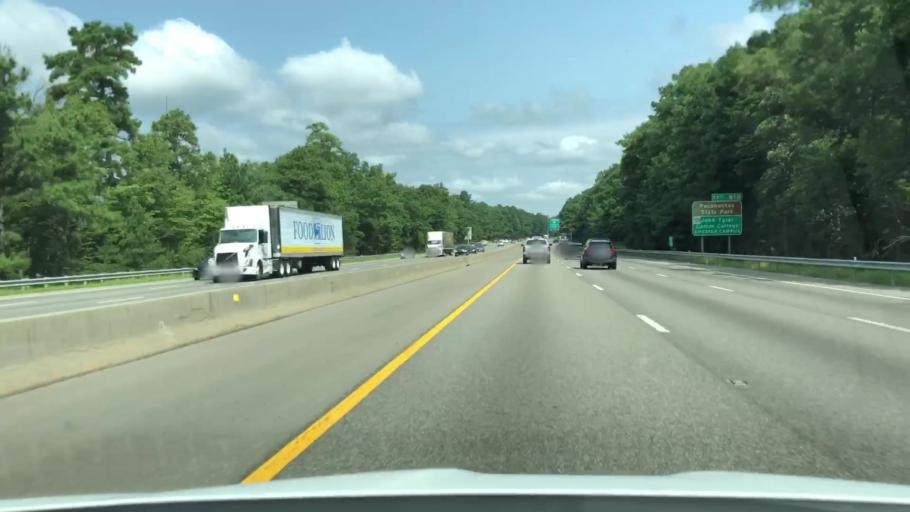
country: US
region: Virginia
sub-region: Chesterfield County
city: Chester
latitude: 37.3347
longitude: -77.4024
